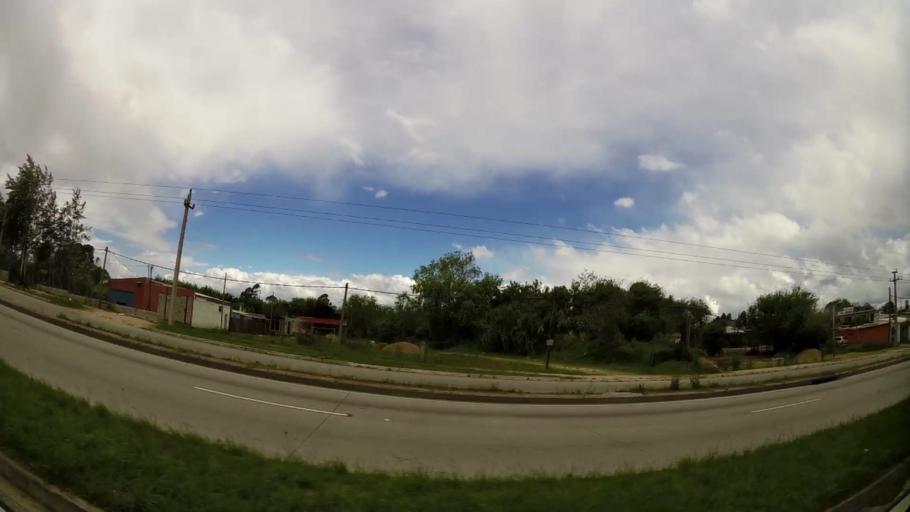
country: UY
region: Canelones
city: Toledo
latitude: -34.7965
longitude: -56.1469
